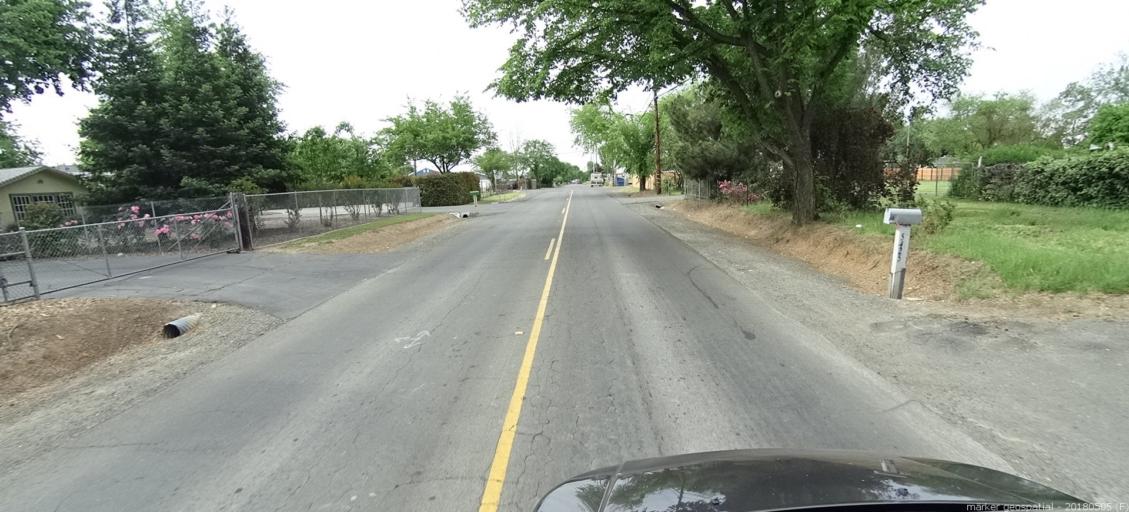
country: US
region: California
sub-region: Sacramento County
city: Rio Linda
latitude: 38.6665
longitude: -121.4384
